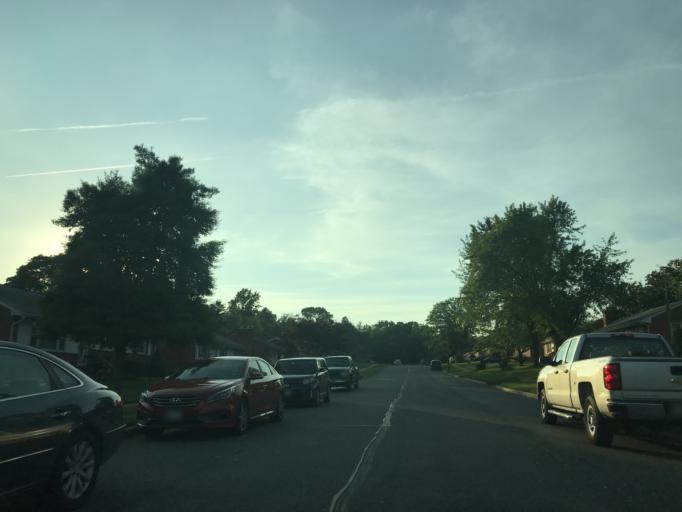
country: US
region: Maryland
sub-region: Harford County
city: Bel Air
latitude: 39.5314
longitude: -76.3552
